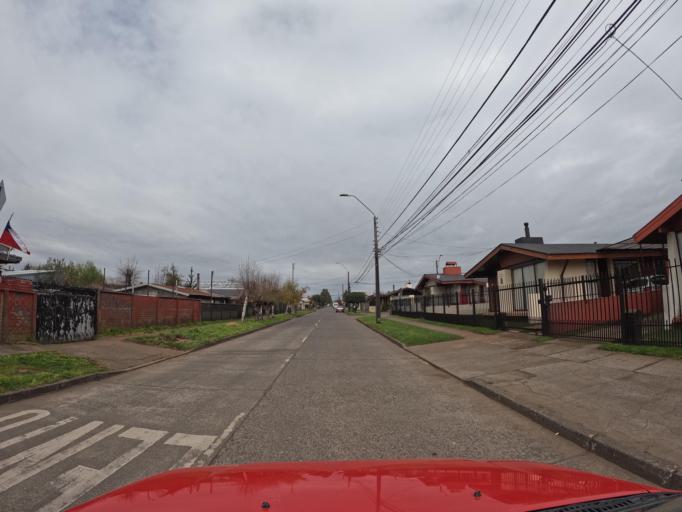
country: CL
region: Araucania
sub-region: Provincia de Malleco
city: Victoria
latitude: -38.2345
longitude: -72.3445
